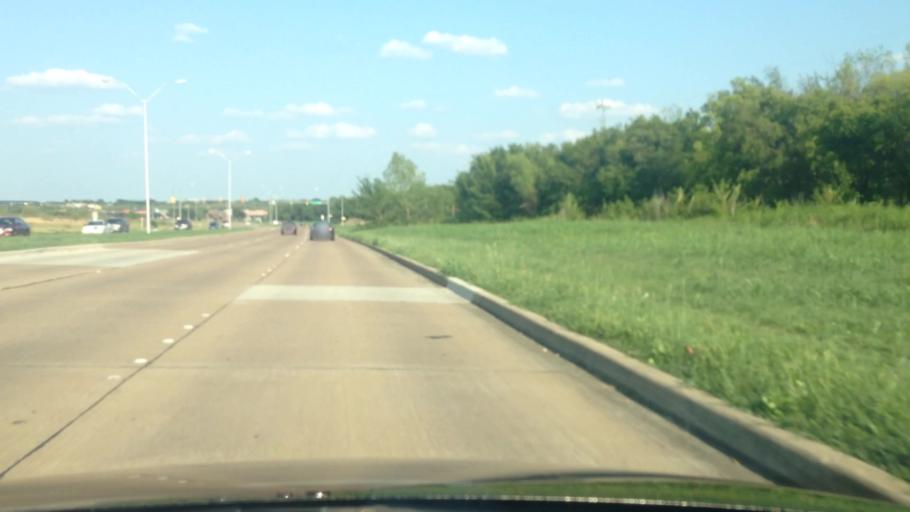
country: US
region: Texas
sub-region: Tarrant County
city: Edgecliff Village
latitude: 32.6482
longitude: -97.3428
